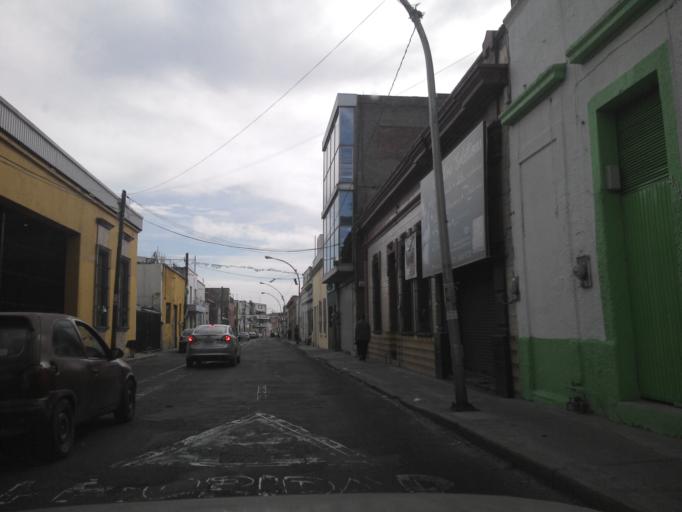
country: MX
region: Jalisco
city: Guadalajara
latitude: 20.6712
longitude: -103.3526
